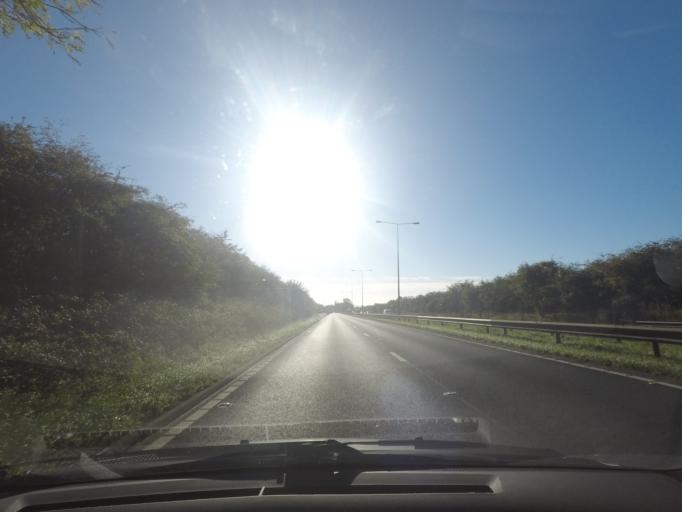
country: GB
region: England
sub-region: East Riding of Yorkshire
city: Welton
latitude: 53.7395
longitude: -0.5632
